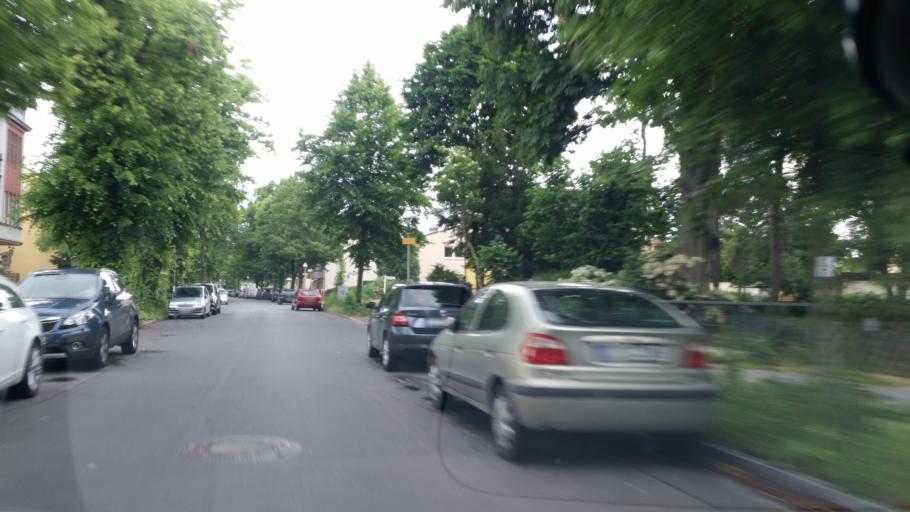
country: DE
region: Berlin
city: Lichtenrade
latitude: 52.3964
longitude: 13.4109
